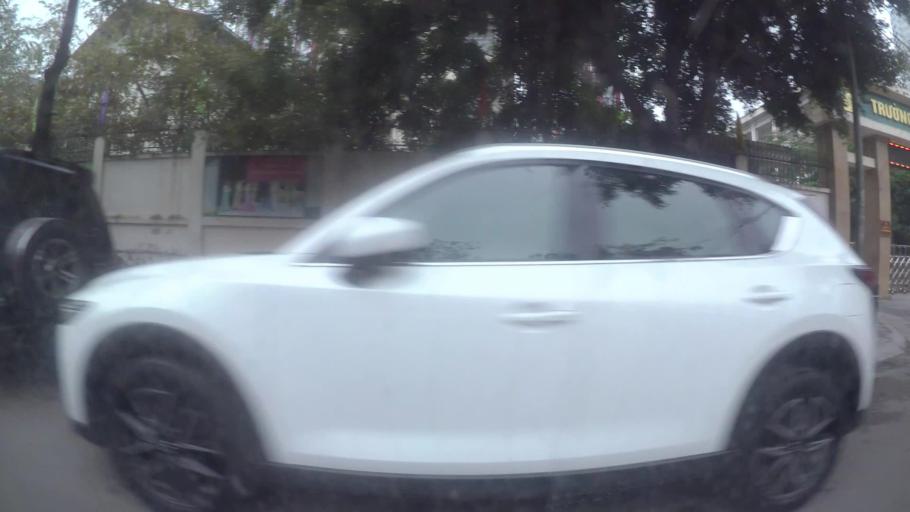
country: VN
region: Ha Noi
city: Cau Dien
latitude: 21.0339
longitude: 105.7831
